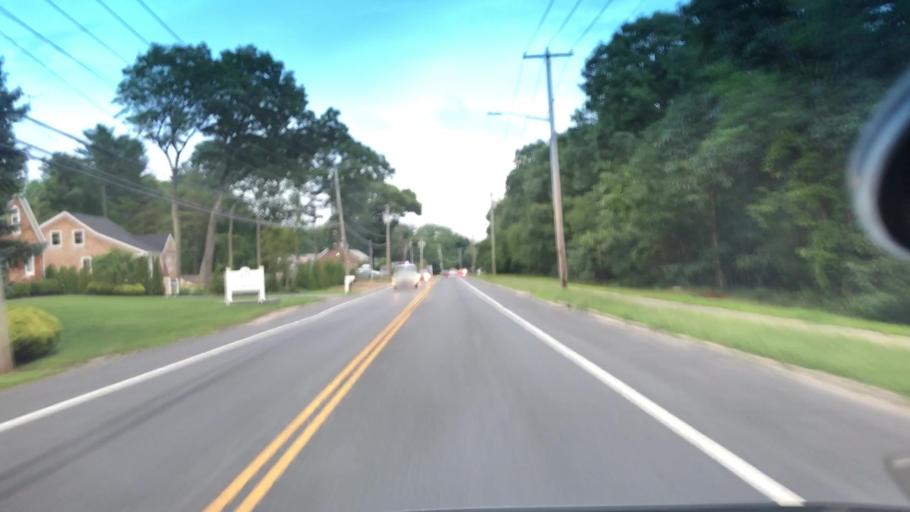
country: US
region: New York
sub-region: Suffolk County
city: Wading River
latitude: 40.9440
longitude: -72.8500
